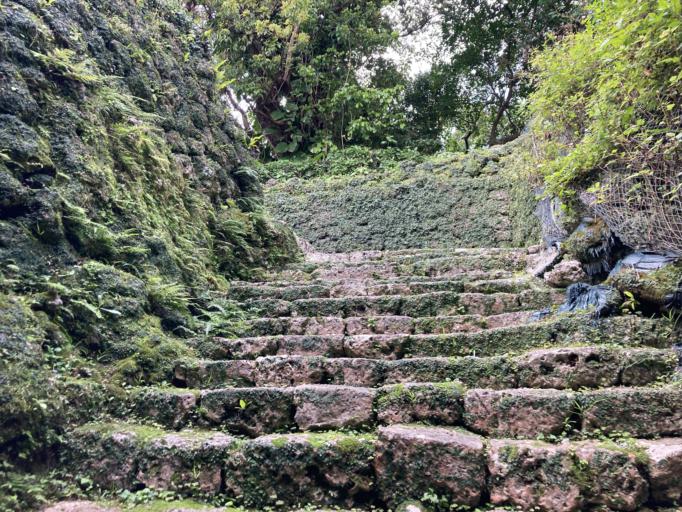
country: JP
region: Okinawa
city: Ginowan
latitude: 26.1855
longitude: 127.7605
